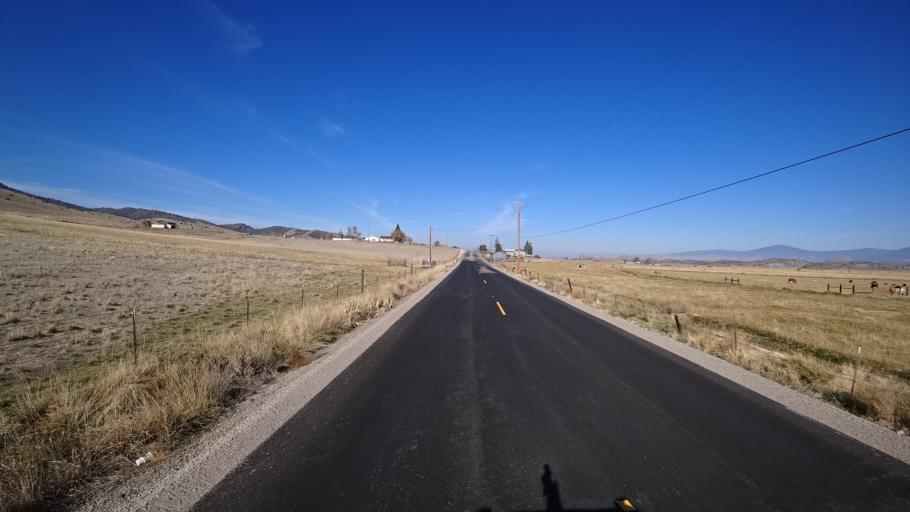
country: US
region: California
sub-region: Siskiyou County
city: Montague
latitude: 41.6052
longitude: -122.5303
